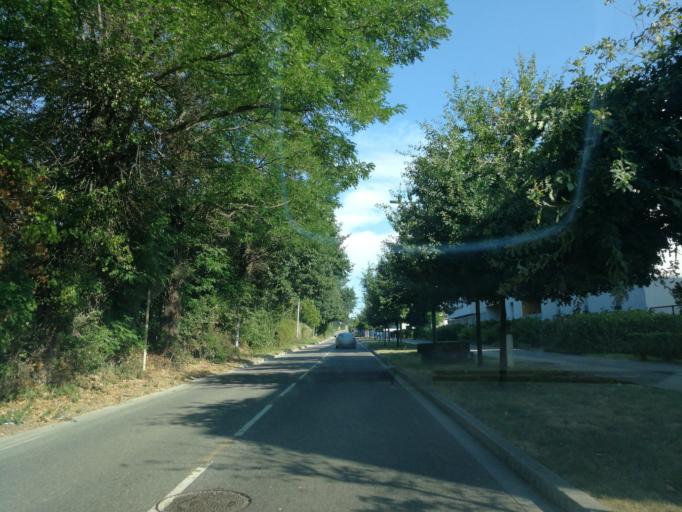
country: FR
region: Midi-Pyrenees
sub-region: Departement de la Haute-Garonne
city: Balma
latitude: 43.6268
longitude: 1.4932
